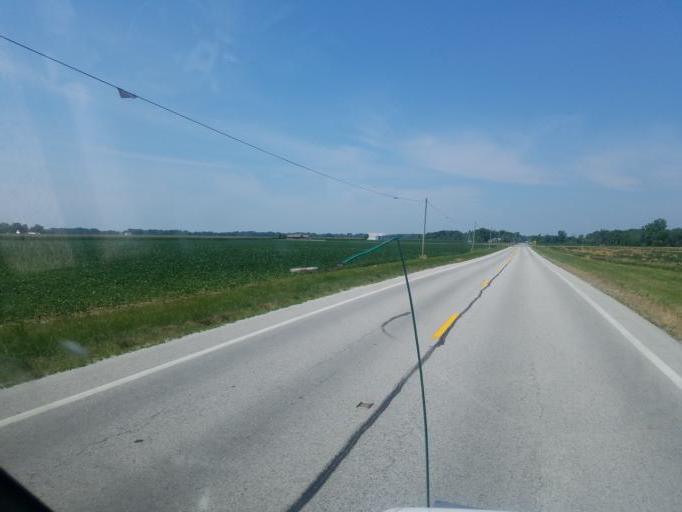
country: US
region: Ohio
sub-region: Auglaize County
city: Saint Marys
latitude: 40.4906
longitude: -84.4345
